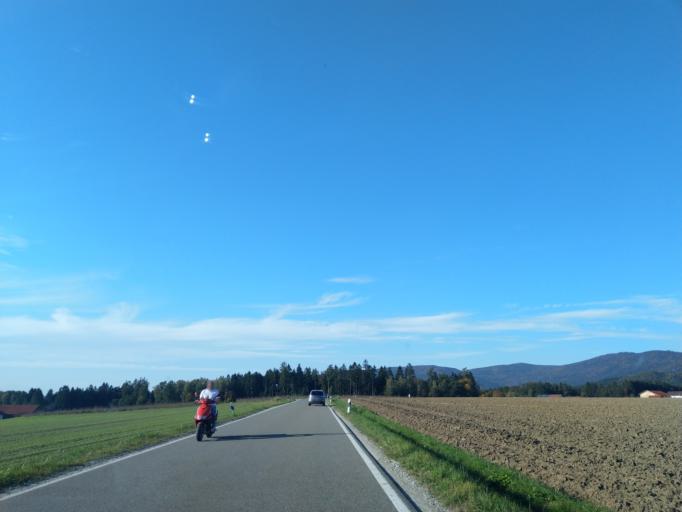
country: DE
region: Bavaria
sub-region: Lower Bavaria
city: Bernried
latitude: 48.8852
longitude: 12.8966
